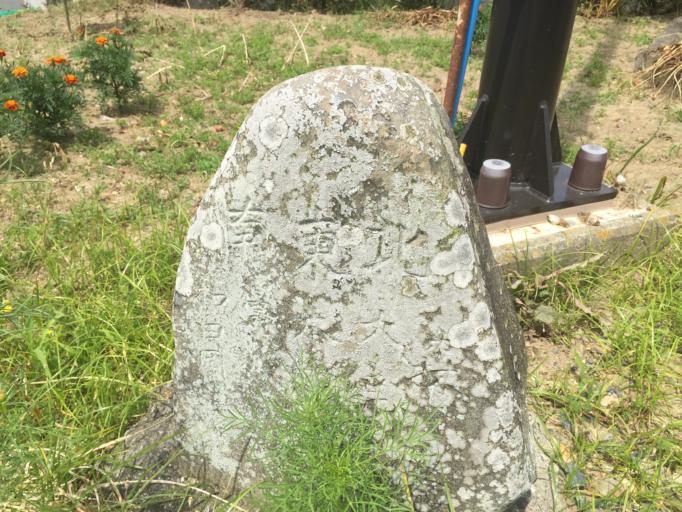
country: JP
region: Shizuoka
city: Mori
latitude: 34.8064
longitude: 137.9497
